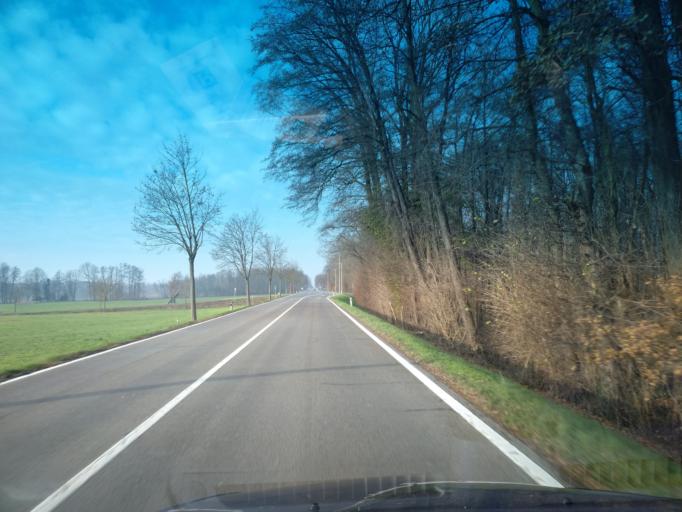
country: AT
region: Styria
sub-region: Politischer Bezirk Leibnitz
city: Strass in Steiermark
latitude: 46.7216
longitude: 15.6239
